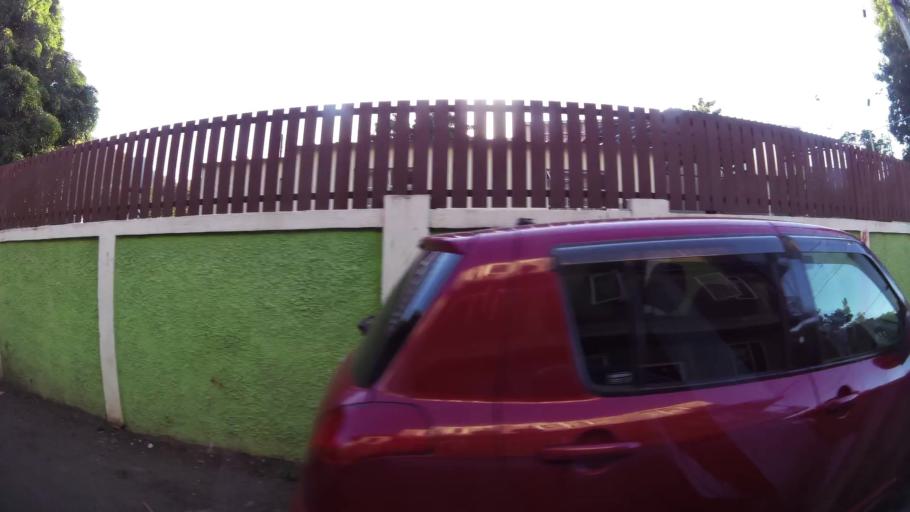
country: MU
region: Port Louis
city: Port Louis
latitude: -20.1777
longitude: 57.5129
